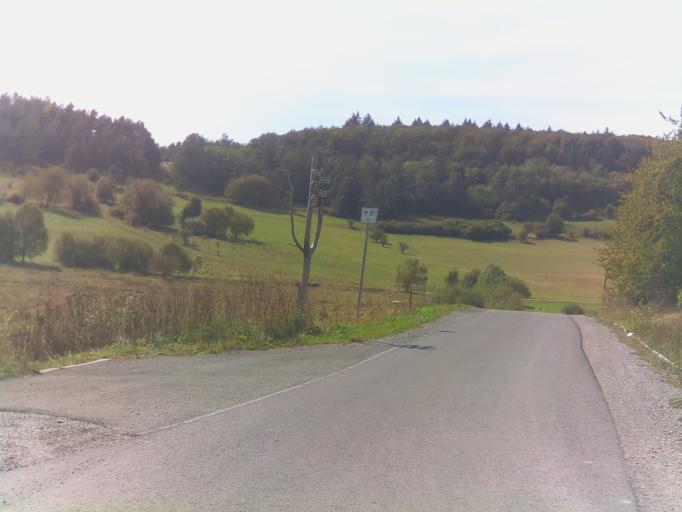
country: DE
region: Thuringia
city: Christes
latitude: 50.6421
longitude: 10.4661
